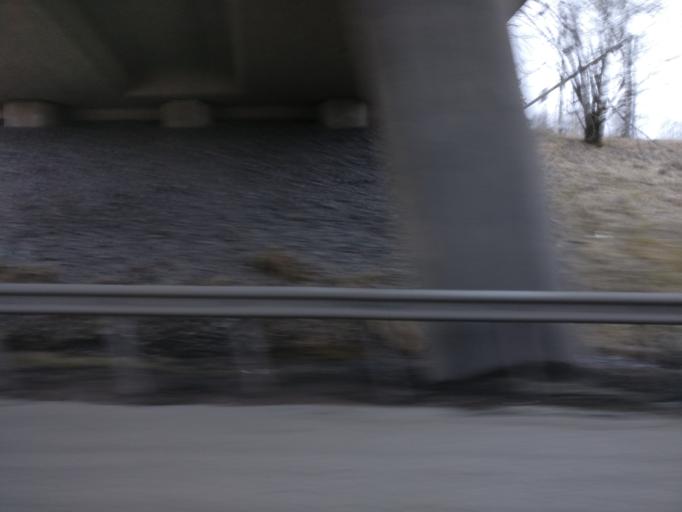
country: FI
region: Uusimaa
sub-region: Helsinki
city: Nurmijaervi
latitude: 60.3385
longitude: 24.8169
